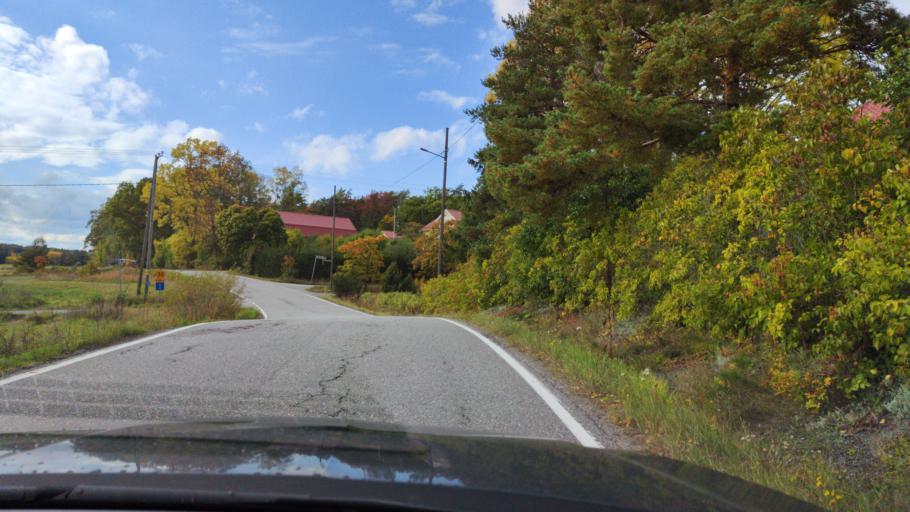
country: FI
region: Varsinais-Suomi
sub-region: Aboland-Turunmaa
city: Pargas
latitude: 60.3471
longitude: 22.1987
